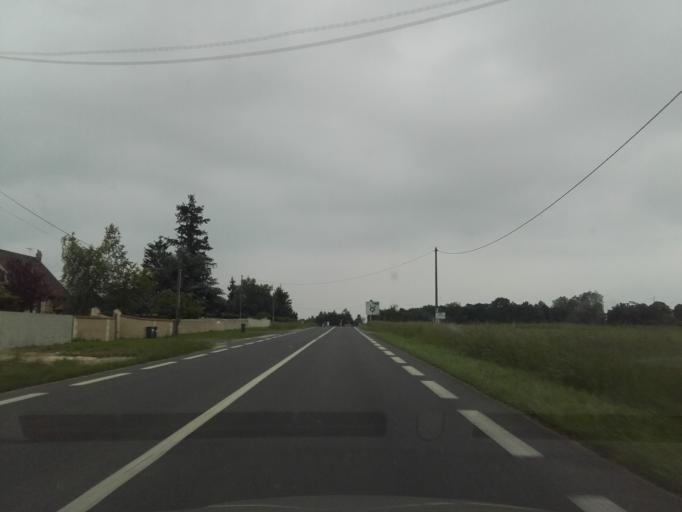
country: FR
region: Centre
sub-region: Departement d'Indre-et-Loire
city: Chanceaux-sur-Choisille
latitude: 47.4529
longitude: 0.6963
